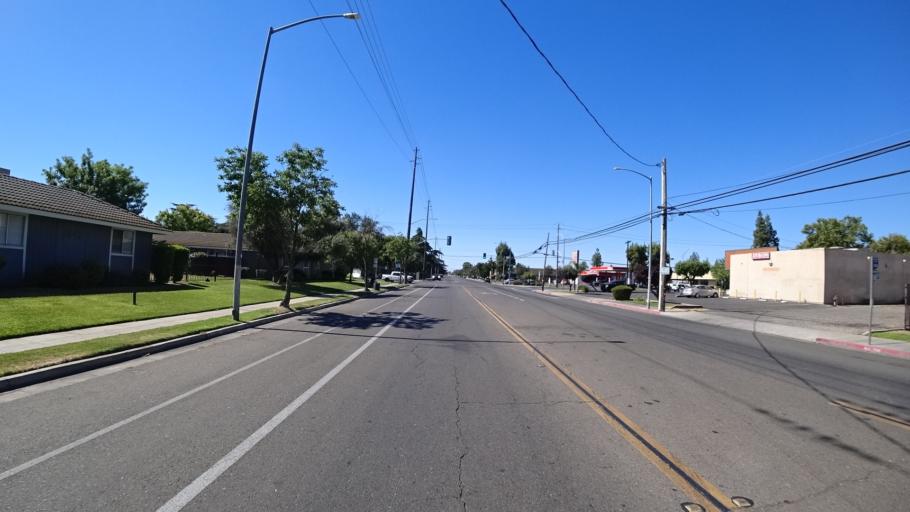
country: US
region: California
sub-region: Fresno County
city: Fresno
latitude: 36.7871
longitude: -119.8354
